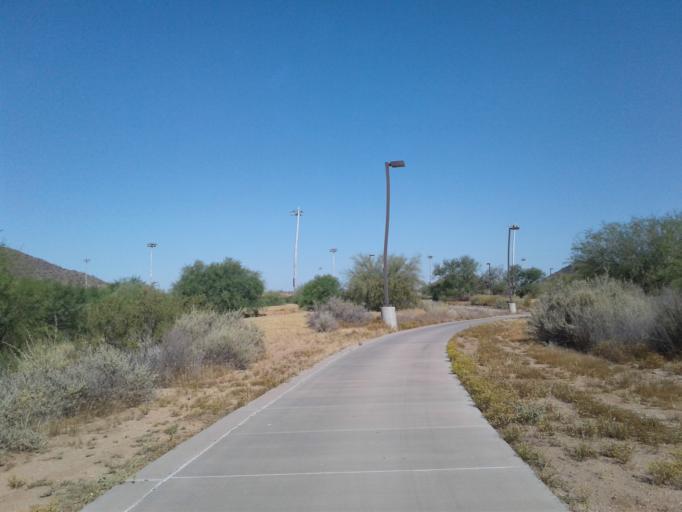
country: US
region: Arizona
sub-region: Maricopa County
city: Cave Creek
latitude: 33.6820
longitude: -112.0250
